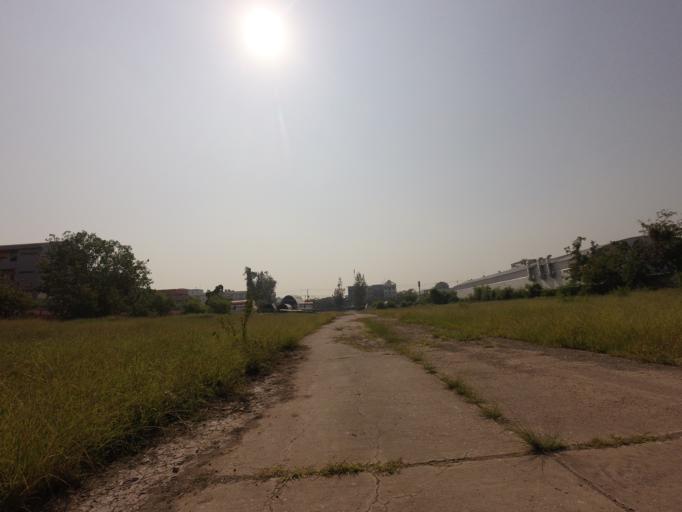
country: TH
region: Bangkok
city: Bang Kapi
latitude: 13.7659
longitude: 100.6515
